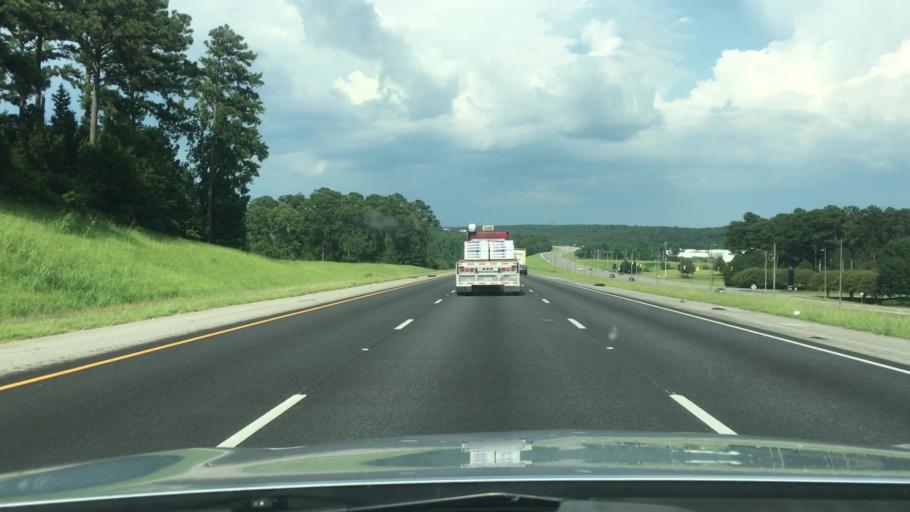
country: US
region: Alabama
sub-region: Tuscaloosa County
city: Vance
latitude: 33.1893
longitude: -87.2637
